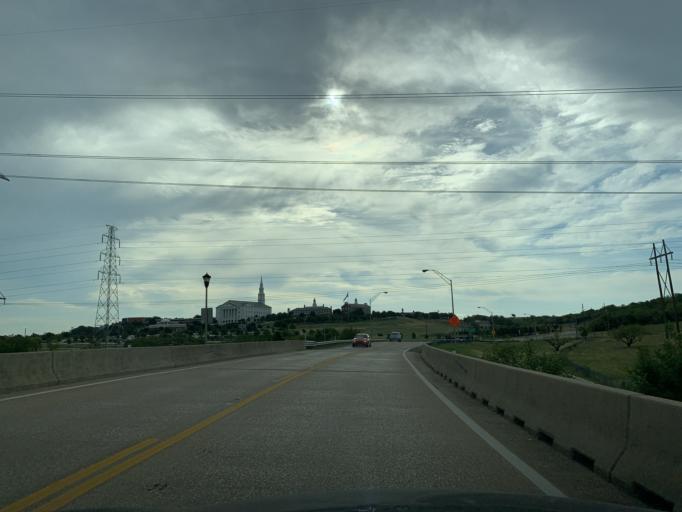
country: US
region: Texas
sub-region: Dallas County
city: Grand Prairie
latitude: 32.7080
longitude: -96.9551
